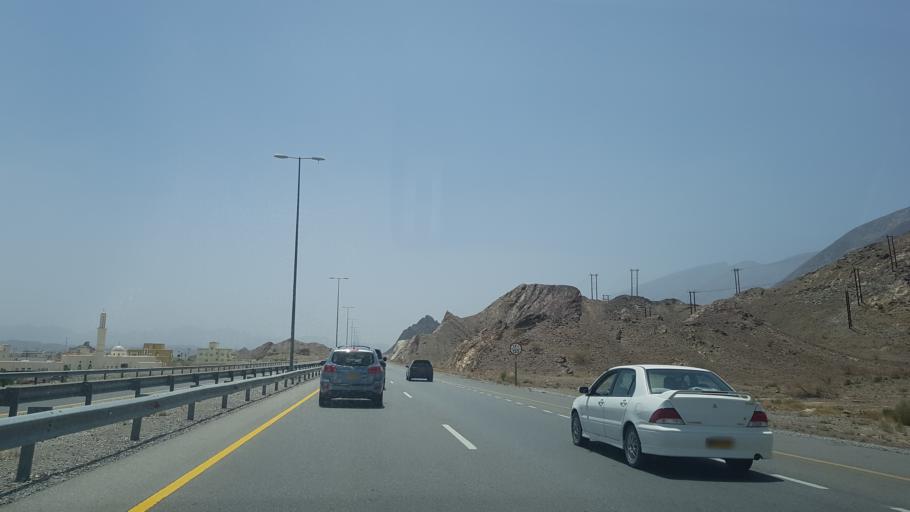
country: OM
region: Muhafazat ad Dakhiliyah
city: Sufalat Sama'il
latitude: 23.2986
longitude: 57.9408
